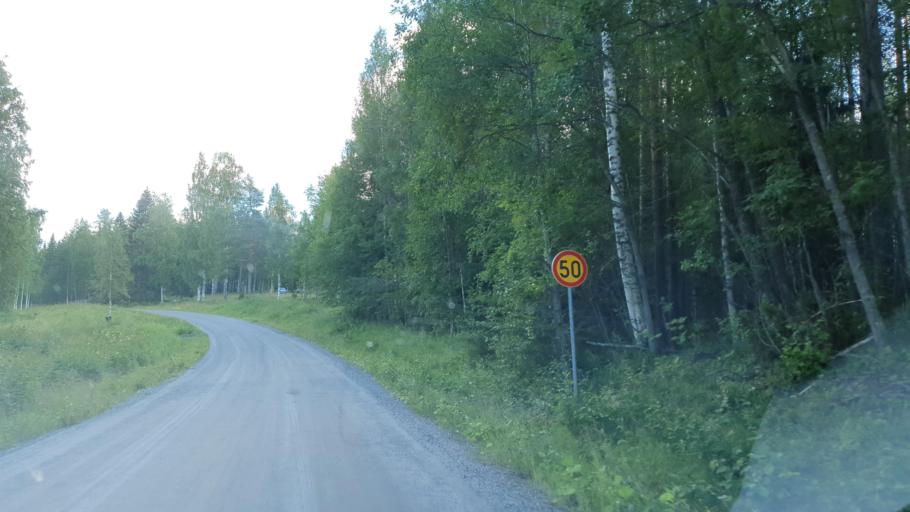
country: FI
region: Kainuu
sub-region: Kehys-Kainuu
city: Kuhmo
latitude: 64.0953
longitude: 29.4163
